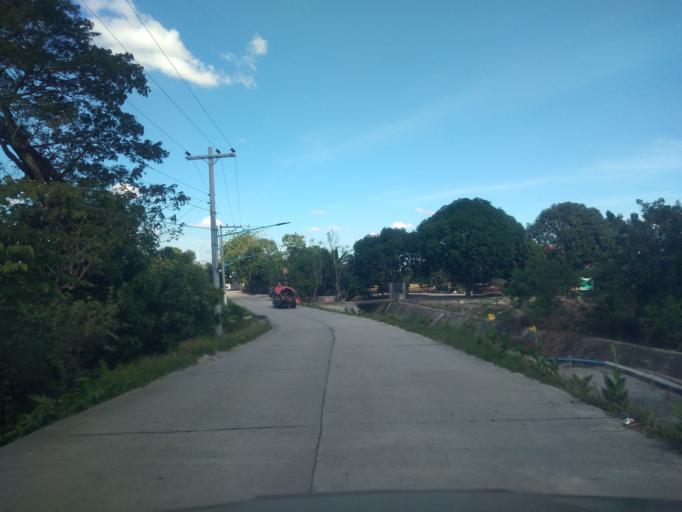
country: PH
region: Central Luzon
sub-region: Province of Pampanga
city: Bacolor
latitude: 15.0055
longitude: 120.6480
